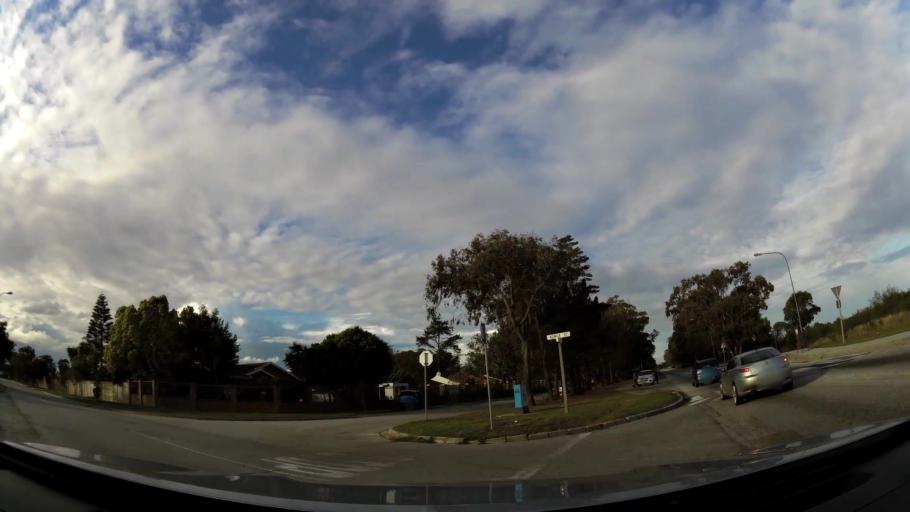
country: ZA
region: Eastern Cape
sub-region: Nelson Mandela Bay Metropolitan Municipality
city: Port Elizabeth
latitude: -33.9582
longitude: 25.4953
